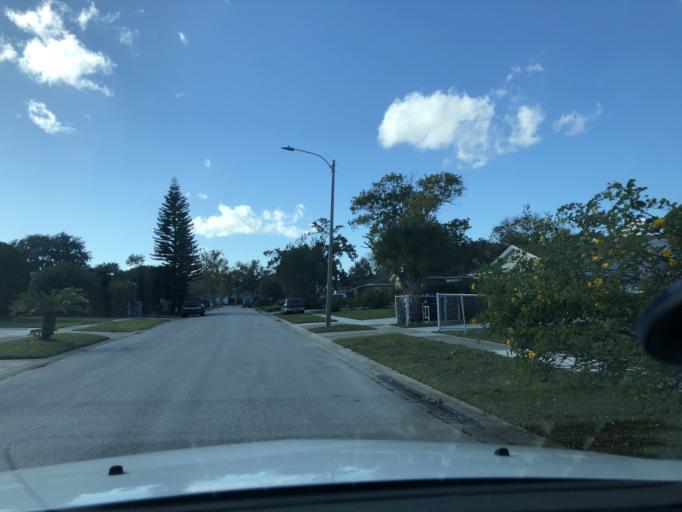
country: US
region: Florida
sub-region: Orange County
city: Oak Ridge
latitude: 28.4777
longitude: -81.4356
